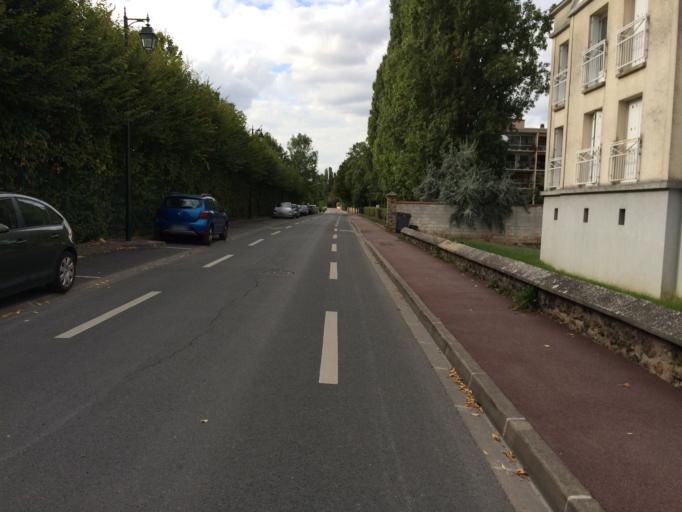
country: FR
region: Ile-de-France
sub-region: Departement de l'Essonne
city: Soisy-sur-Seine
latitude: 48.6494
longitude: 2.4420
